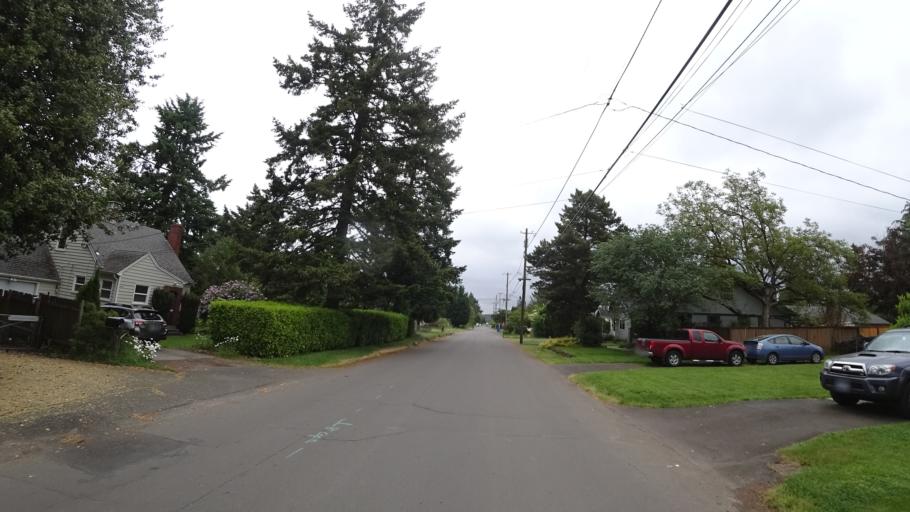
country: US
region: Oregon
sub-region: Multnomah County
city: Portland
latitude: 45.5525
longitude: -122.6064
